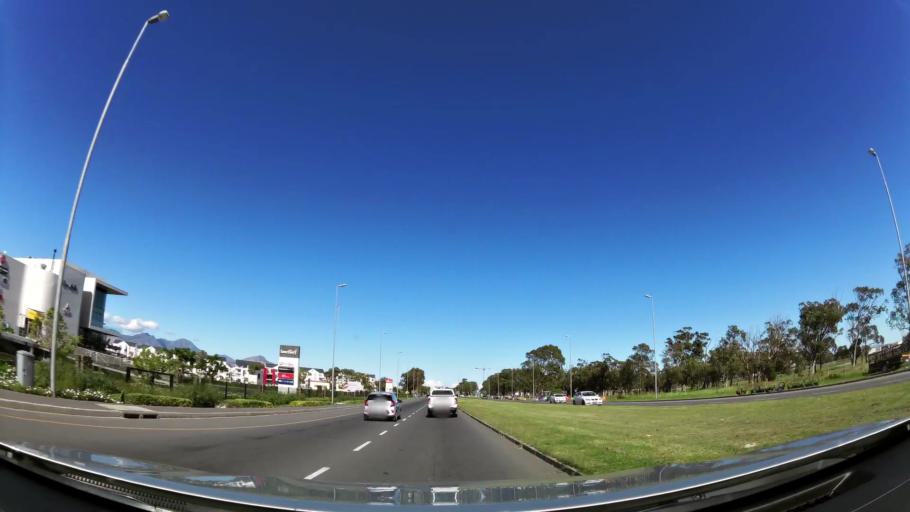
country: ZA
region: Western Cape
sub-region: Cape Winelands District Municipality
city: Stellenbosch
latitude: -34.0875
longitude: 18.8199
